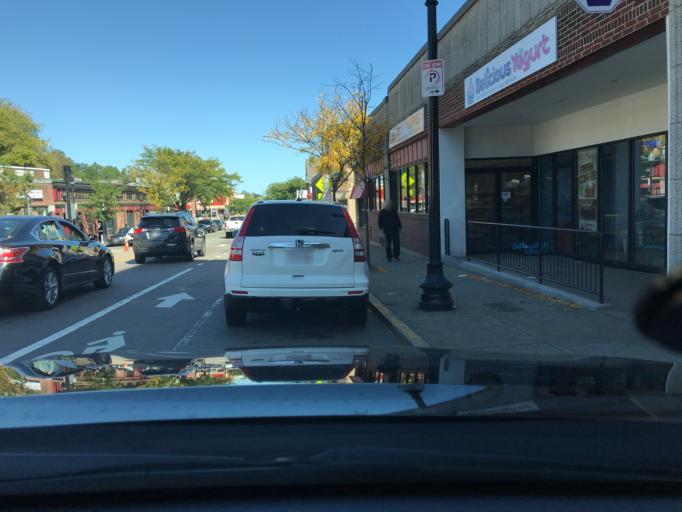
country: US
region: Massachusetts
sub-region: Suffolk County
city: Jamaica Plain
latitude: 42.2868
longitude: -71.1277
